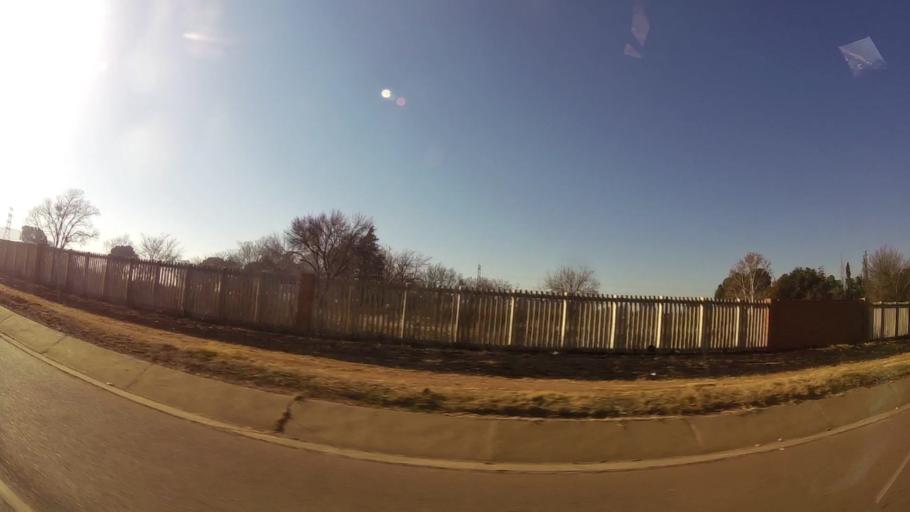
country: ZA
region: Gauteng
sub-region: City of Tshwane Metropolitan Municipality
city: Centurion
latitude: -25.8370
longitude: 28.1119
